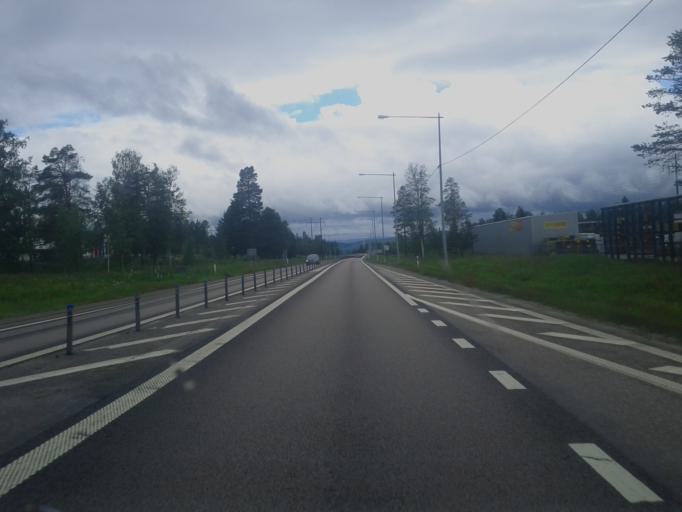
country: SE
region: Vaesternorrland
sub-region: Haernoesands Kommun
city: Haernoesand
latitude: 62.6497
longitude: 17.8940
